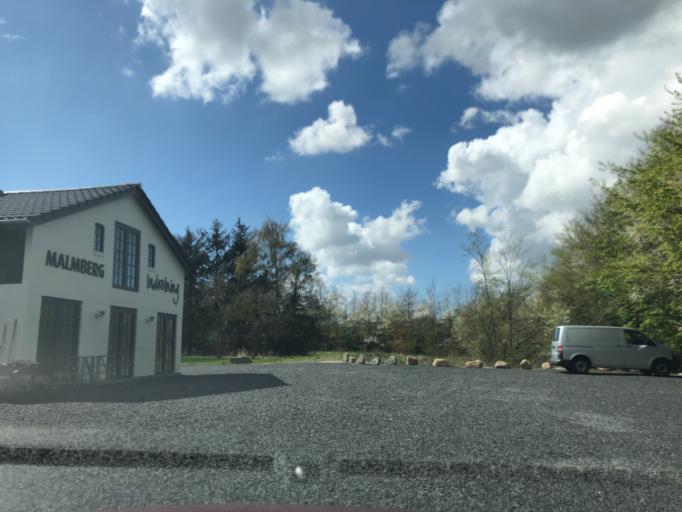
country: DK
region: Capital Region
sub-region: Gribskov Kommune
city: Helsinge
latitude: 56.0203
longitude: 12.1775
